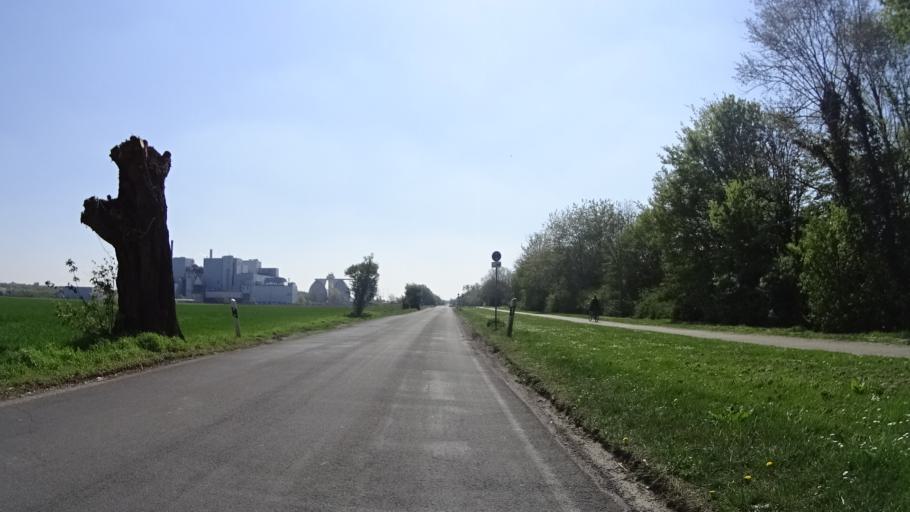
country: DE
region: North Rhine-Westphalia
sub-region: Regierungsbezirk Dusseldorf
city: Krefeld
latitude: 51.3847
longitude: 6.6325
